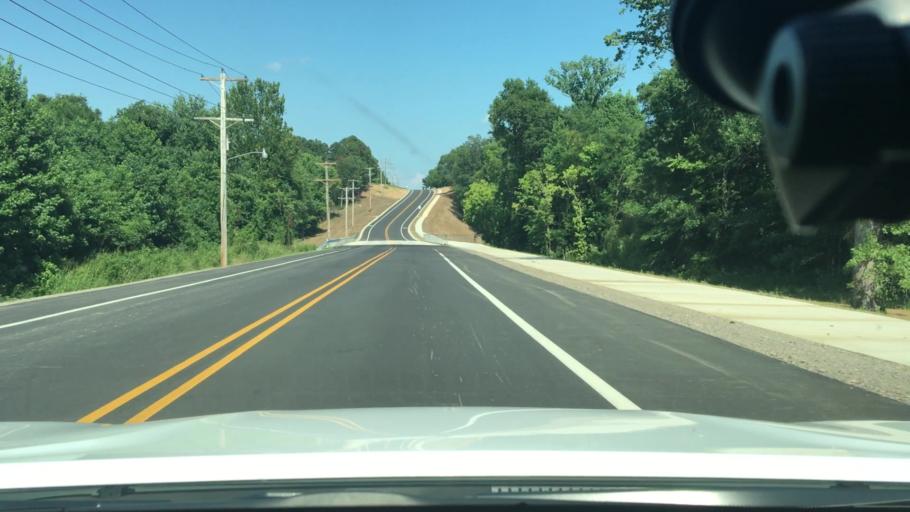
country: US
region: Arkansas
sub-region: Johnson County
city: Clarksville
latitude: 35.4620
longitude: -93.4986
